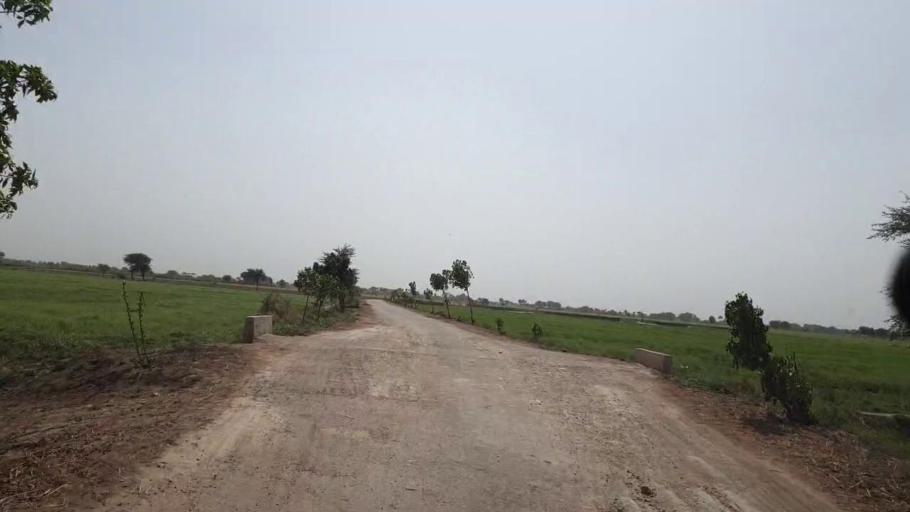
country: PK
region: Sindh
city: Matli
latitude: 25.0486
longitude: 68.6831
